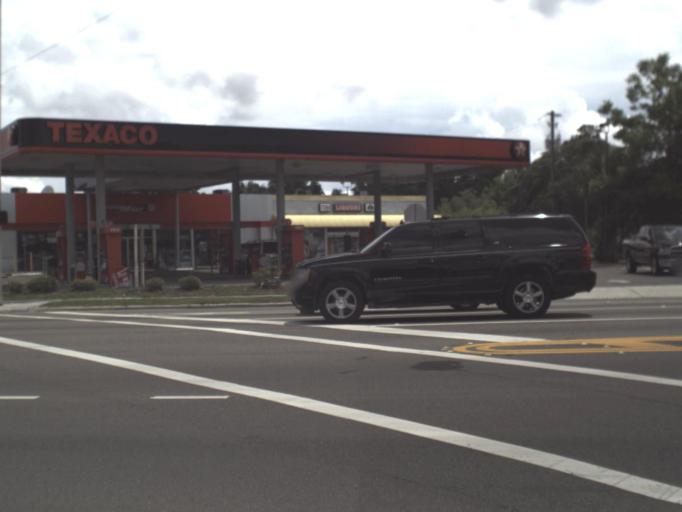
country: US
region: Florida
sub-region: Nassau County
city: Yulee
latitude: 30.6322
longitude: -81.6015
